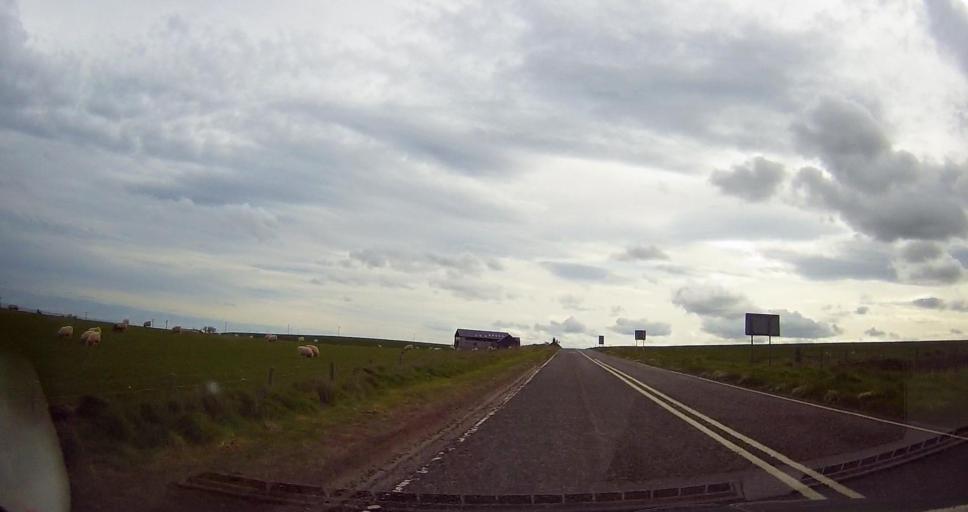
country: GB
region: Scotland
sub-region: Aberdeenshire
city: Stonehaven
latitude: 56.9194
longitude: -2.2108
